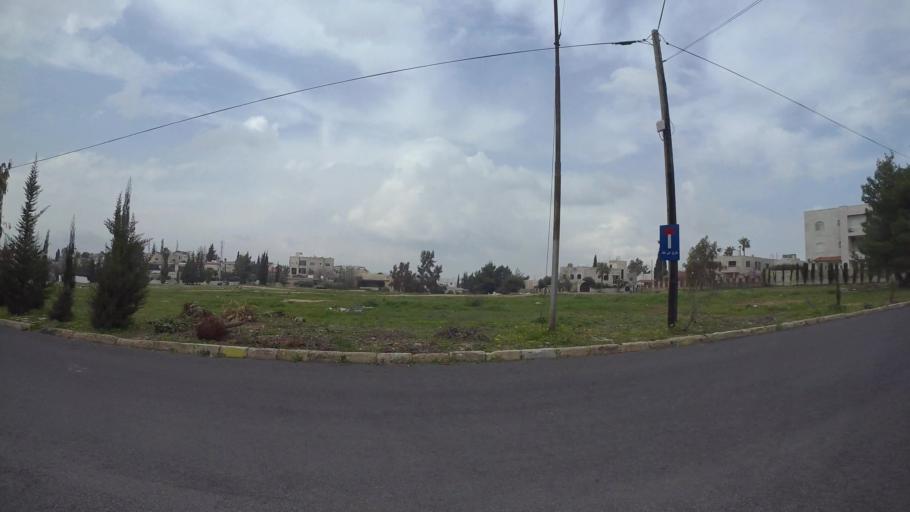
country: JO
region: Amman
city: Umm as Summaq
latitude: 31.8930
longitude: 35.8584
